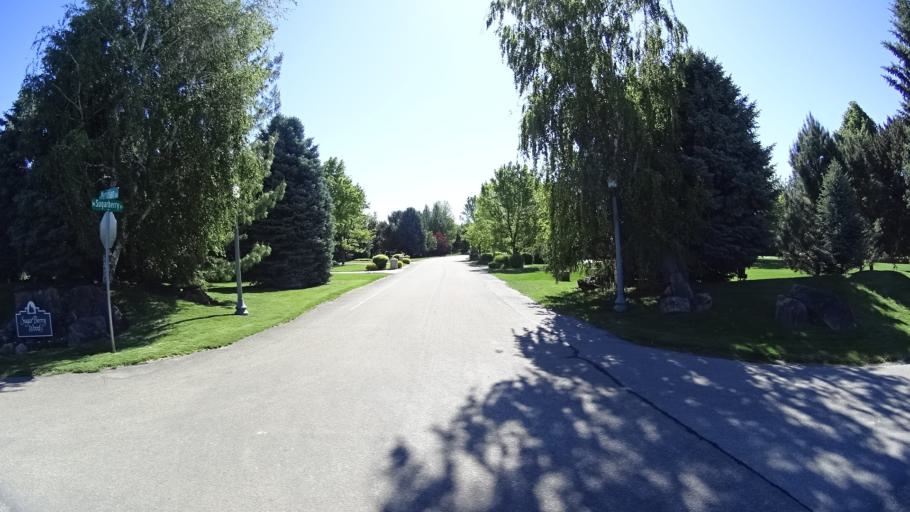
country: US
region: Idaho
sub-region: Ada County
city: Eagle
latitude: 43.6692
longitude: -116.3935
